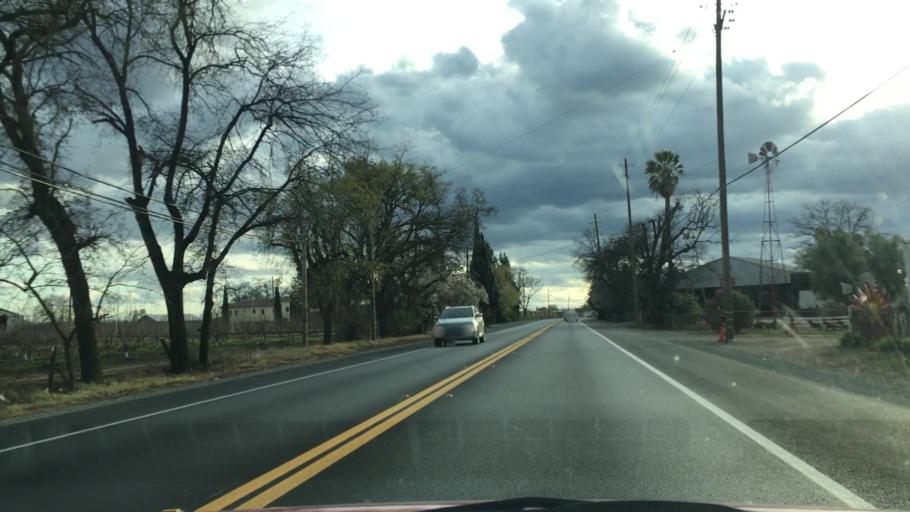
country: US
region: California
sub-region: San Joaquin County
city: Garden Acres
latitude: 38.0042
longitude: -121.2207
